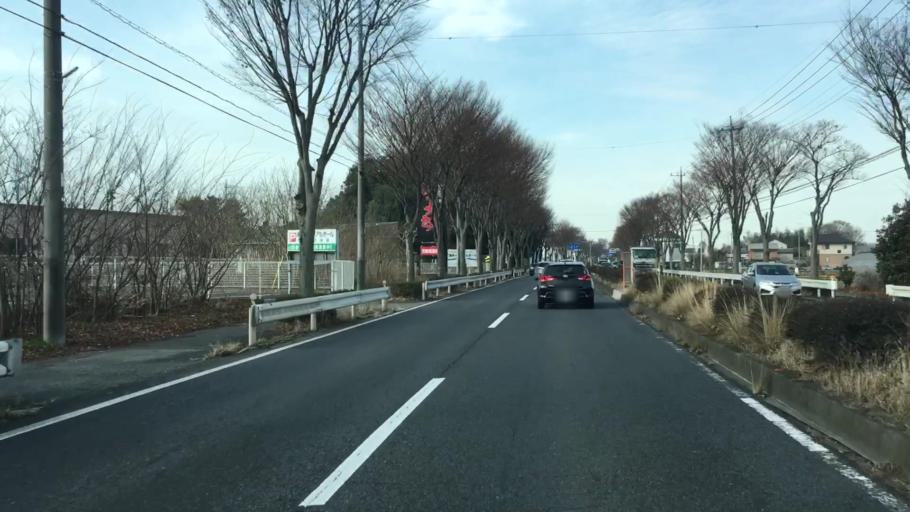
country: JP
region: Gunma
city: Tatebayashi
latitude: 36.2304
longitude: 139.5605
